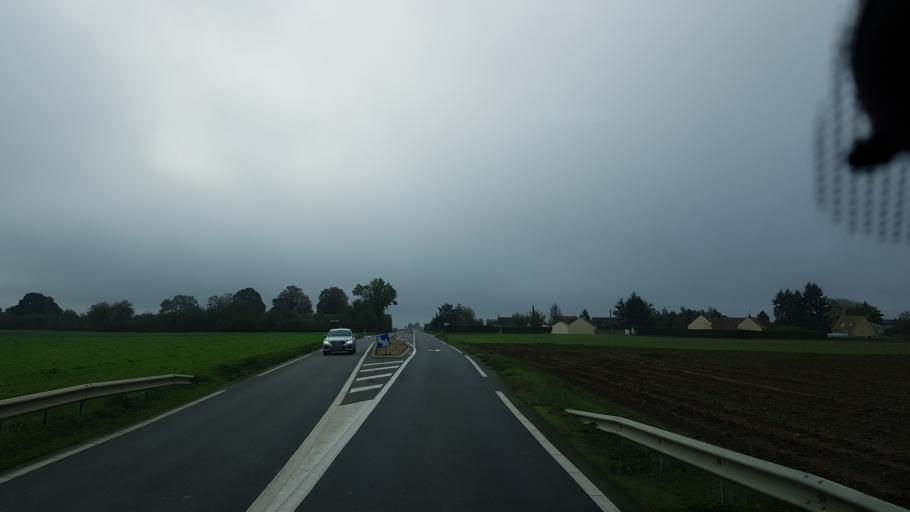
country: FR
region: Ile-de-France
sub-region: Departement de l'Essonne
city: Corbreuse
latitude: 48.4258
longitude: 1.9629
